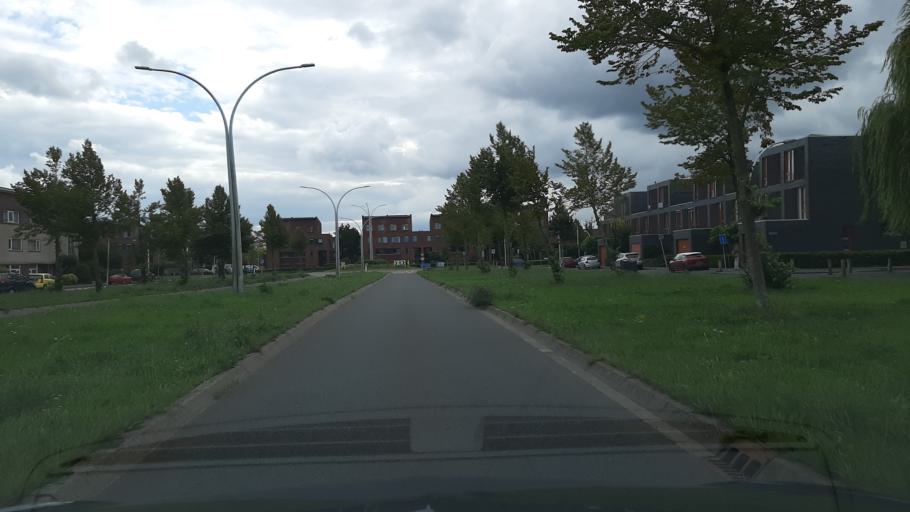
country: NL
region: Overijssel
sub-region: Gemeente Zwolle
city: Zwolle
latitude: 52.5397
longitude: 6.0540
